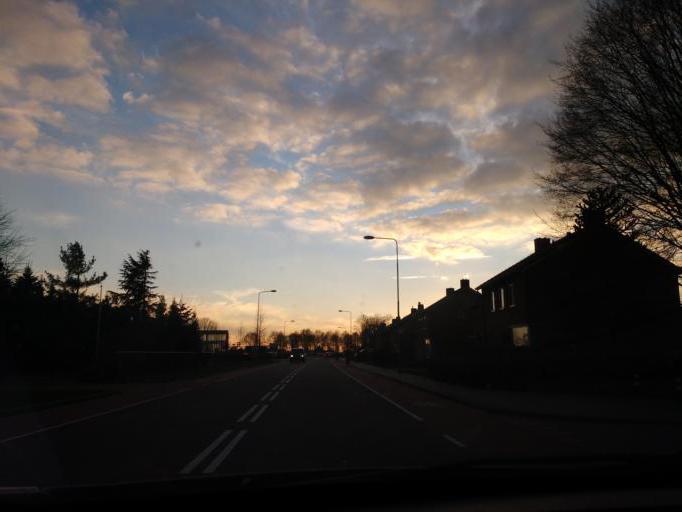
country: NL
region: Limburg
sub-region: Gemeente Venray
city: Venray
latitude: 51.5155
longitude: 5.9666
